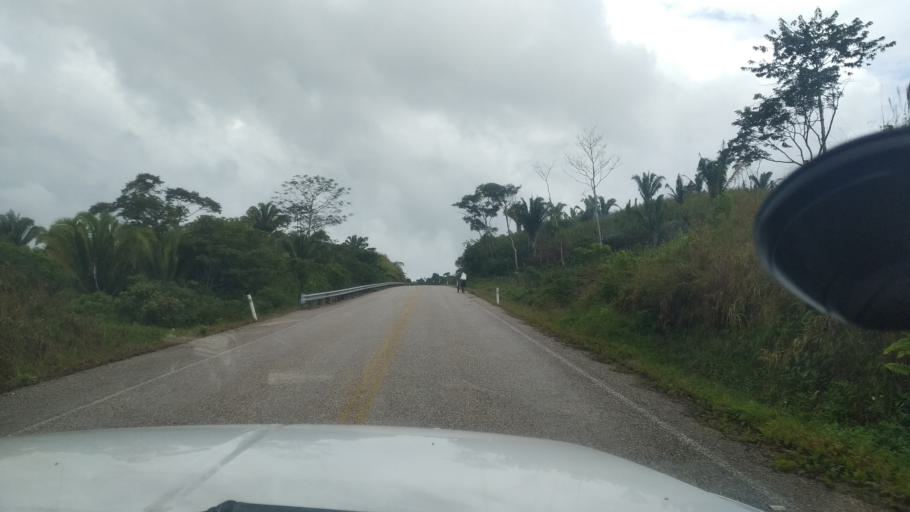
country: GT
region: Peten
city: San Luis
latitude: 16.1947
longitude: -89.1690
